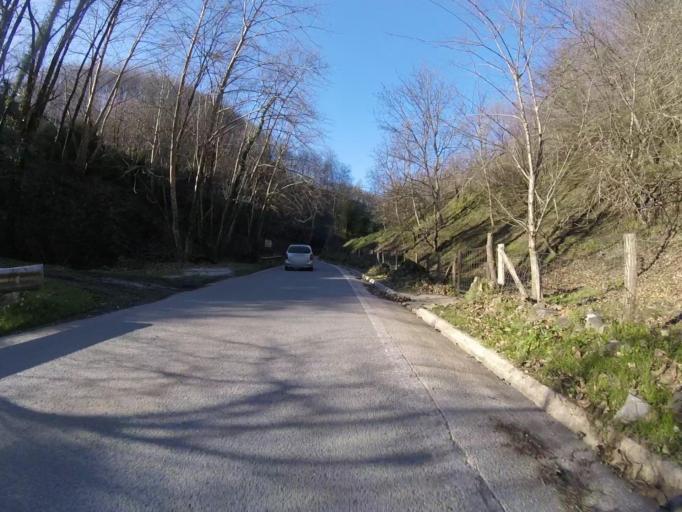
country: ES
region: Navarre
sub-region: Provincia de Navarra
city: Lesaka
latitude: 43.2477
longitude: -1.7195
